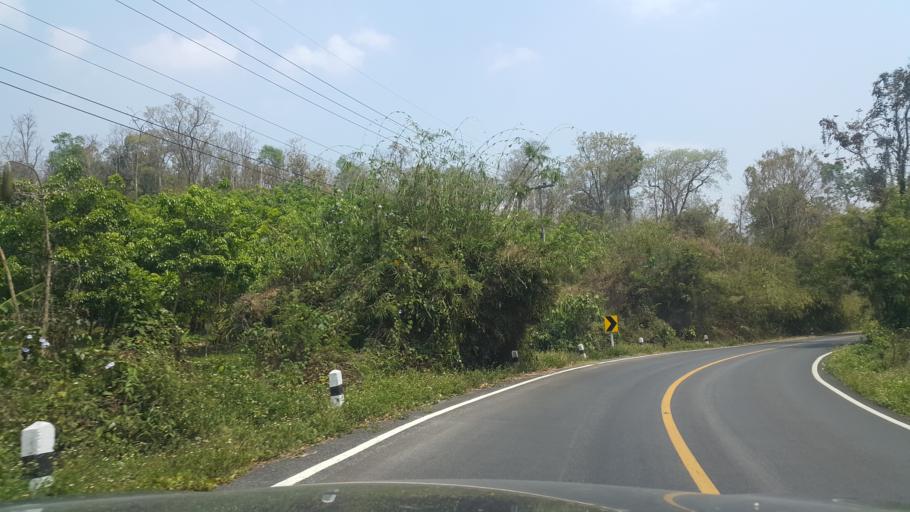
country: TH
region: Lamphun
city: Thung Hua Chang
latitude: 17.9070
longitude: 99.1168
